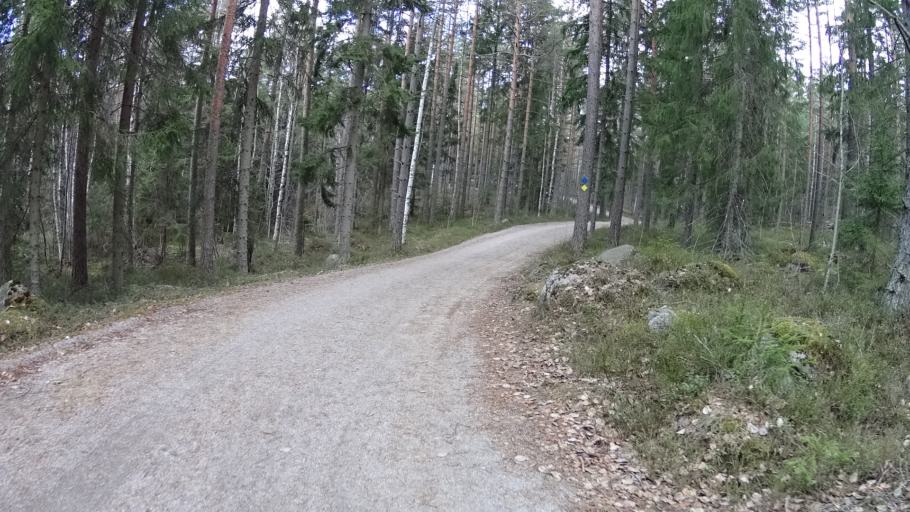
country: FI
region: Uusimaa
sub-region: Helsinki
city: Espoo
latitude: 60.2729
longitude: 24.6234
